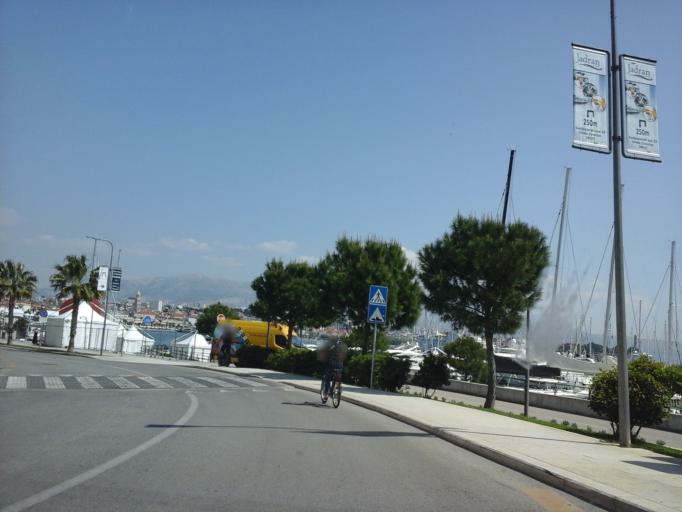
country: HR
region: Splitsko-Dalmatinska
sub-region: Grad Split
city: Split
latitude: 43.5030
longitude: 16.4279
